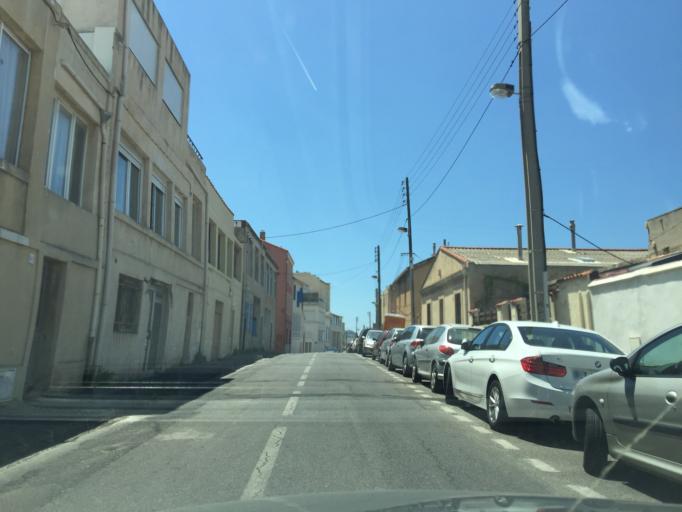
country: FR
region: Provence-Alpes-Cote d'Azur
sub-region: Departement des Bouches-du-Rhone
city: Marseille 08
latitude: 43.2511
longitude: 5.3773
